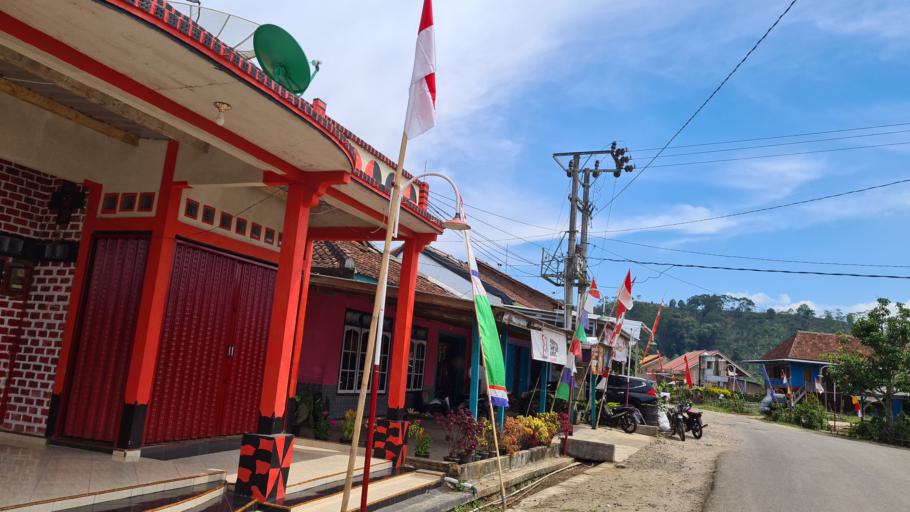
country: ID
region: Lampung
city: Kenali
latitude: -5.0957
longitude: 104.4238
